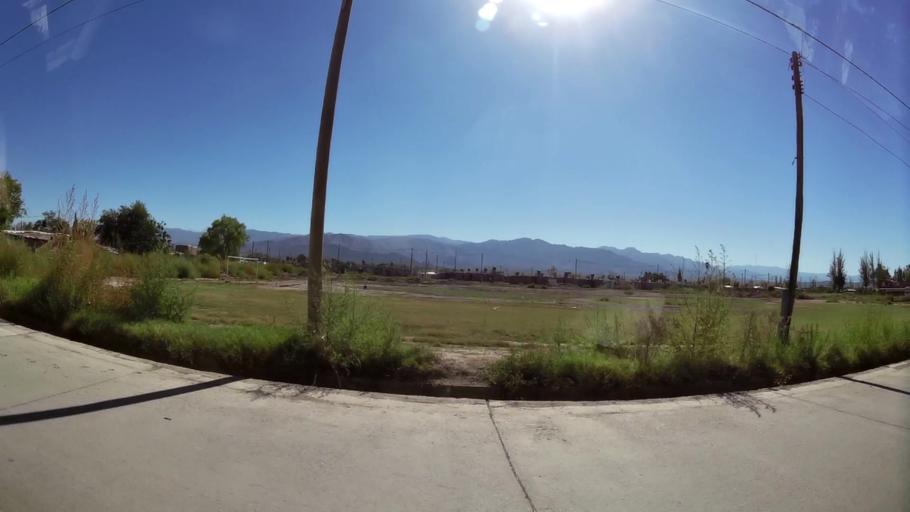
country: AR
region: Mendoza
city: Las Heras
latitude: -32.8345
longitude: -68.8156
